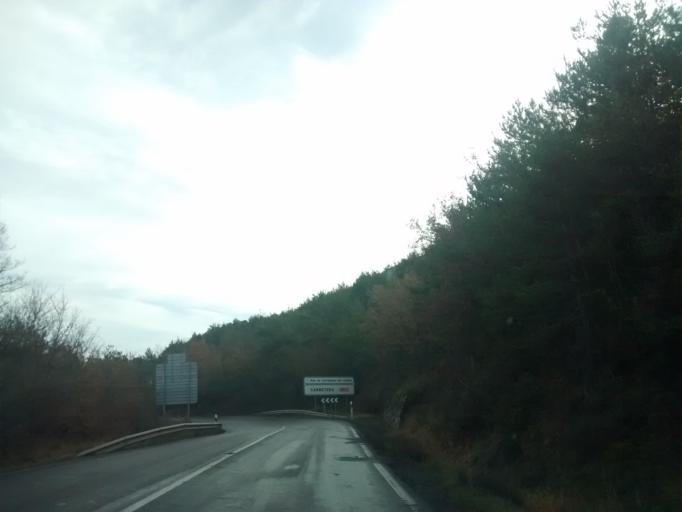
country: ES
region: Aragon
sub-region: Provincia de Huesca
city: Bailo
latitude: 42.5537
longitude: -0.7792
